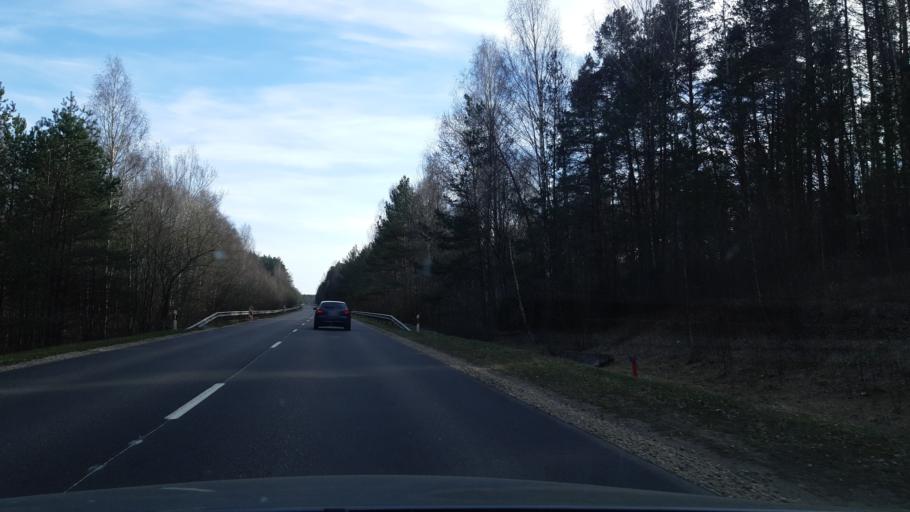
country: LT
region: Alytaus apskritis
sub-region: Alytaus rajonas
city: Daugai
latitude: 54.1574
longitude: 24.2089
